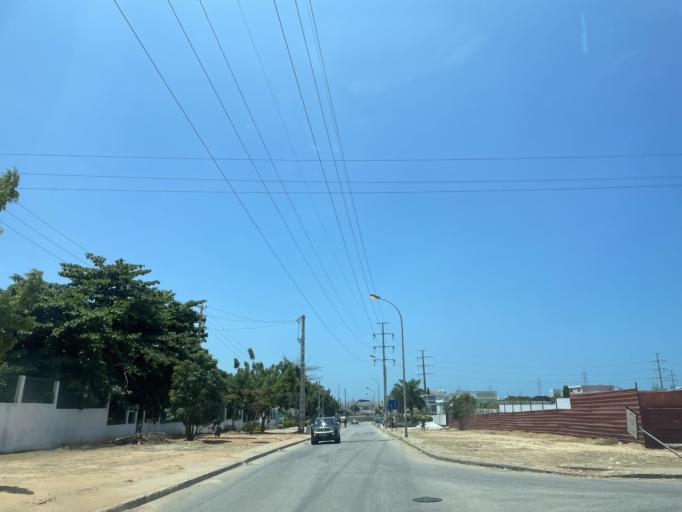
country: AO
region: Luanda
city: Luanda
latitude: -8.9074
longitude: 13.1978
